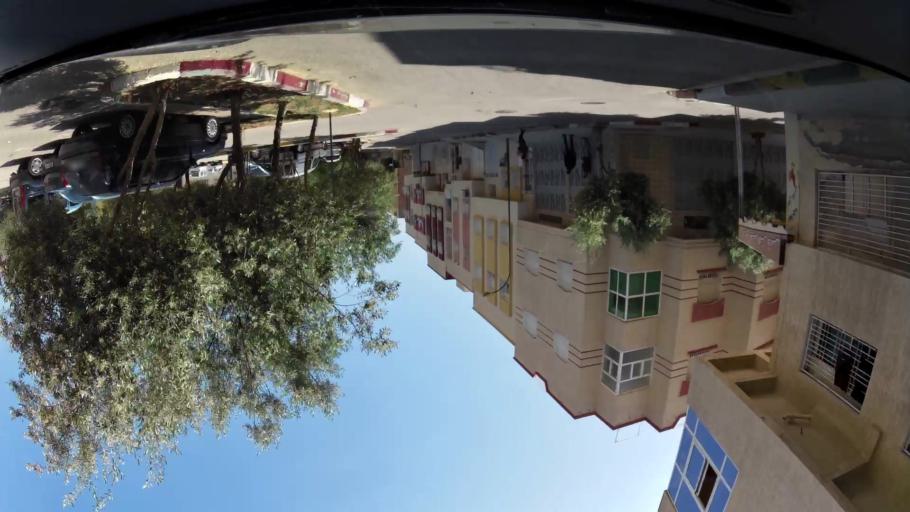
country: MA
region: Fes-Boulemane
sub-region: Fes
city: Fes
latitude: 34.0612
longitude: -5.0257
